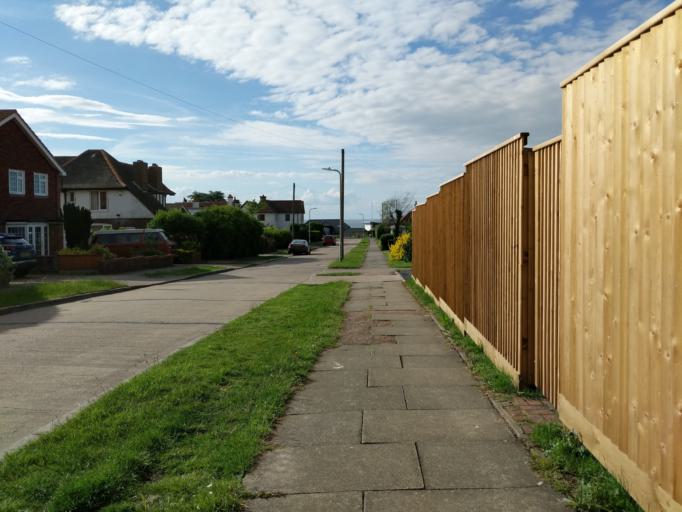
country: GB
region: England
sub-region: Kent
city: Whitstable
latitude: 51.3483
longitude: 1.0101
